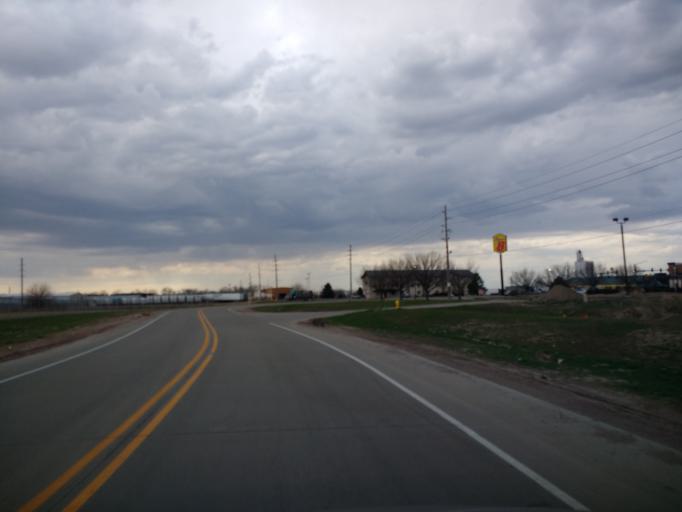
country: US
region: Iowa
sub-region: Woodbury County
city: Sergeant Bluff
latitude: 42.4326
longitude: -96.3768
